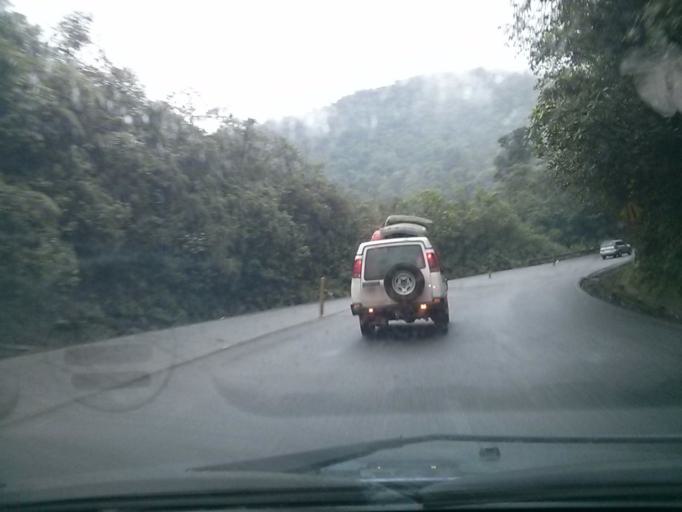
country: CR
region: San Jose
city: Dulce Nombre de Jesus
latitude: 10.0685
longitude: -84.0013
